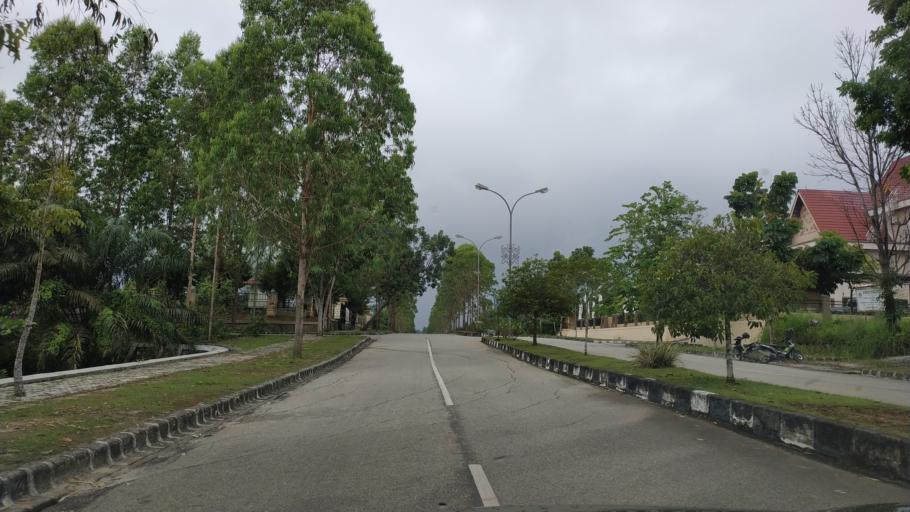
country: ID
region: Riau
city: Pangkalanbunut
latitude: 0.3829
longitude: 101.8277
